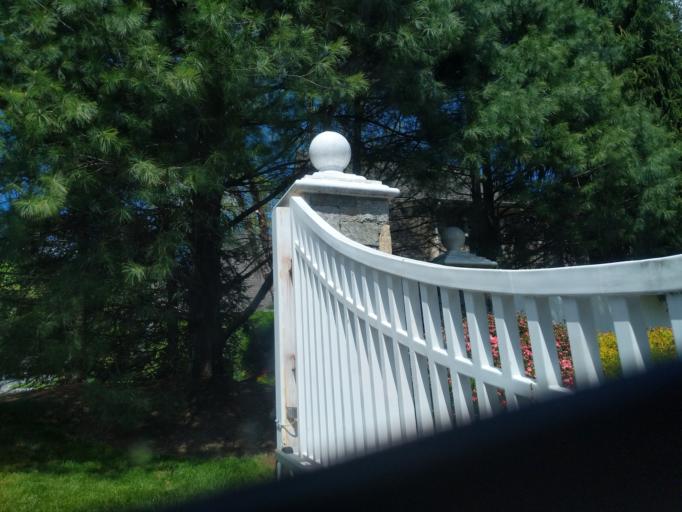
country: US
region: New York
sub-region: Westchester County
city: Tuckahoe
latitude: 40.9582
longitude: -73.7955
